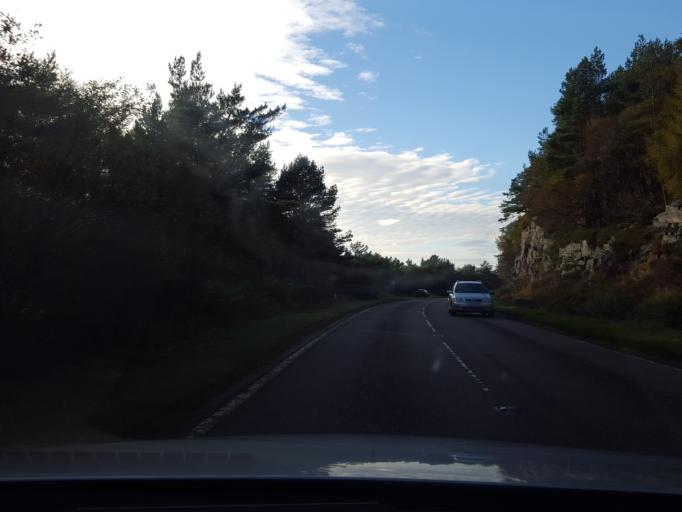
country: GB
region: Scotland
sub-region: Highland
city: Portree
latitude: 57.2834
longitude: -5.6620
